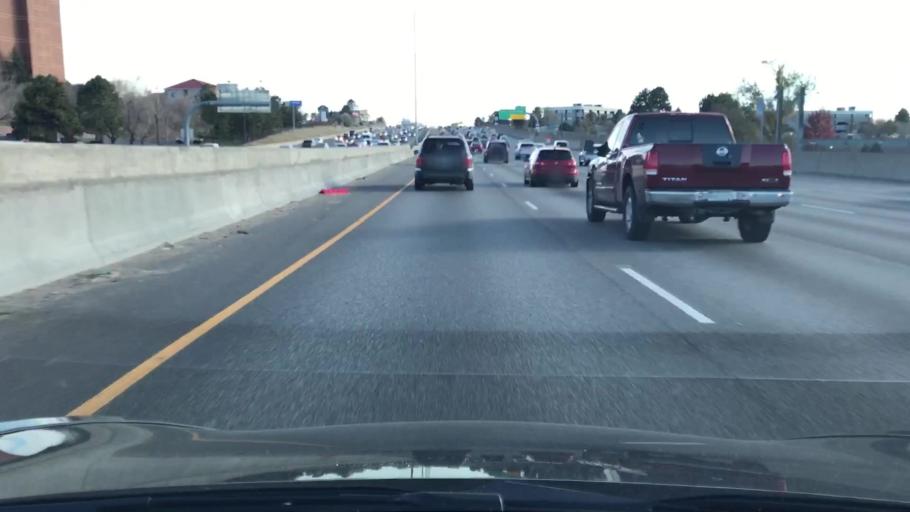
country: US
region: Colorado
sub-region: Arapahoe County
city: Centennial
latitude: 39.5908
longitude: -104.8833
